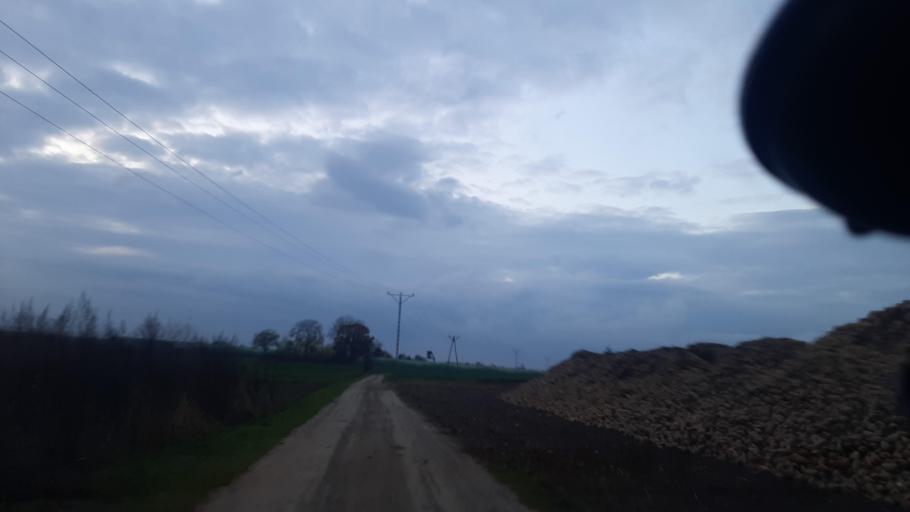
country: PL
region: Lublin Voivodeship
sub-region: Powiat lubelski
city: Jastkow
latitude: 51.3305
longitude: 22.3945
